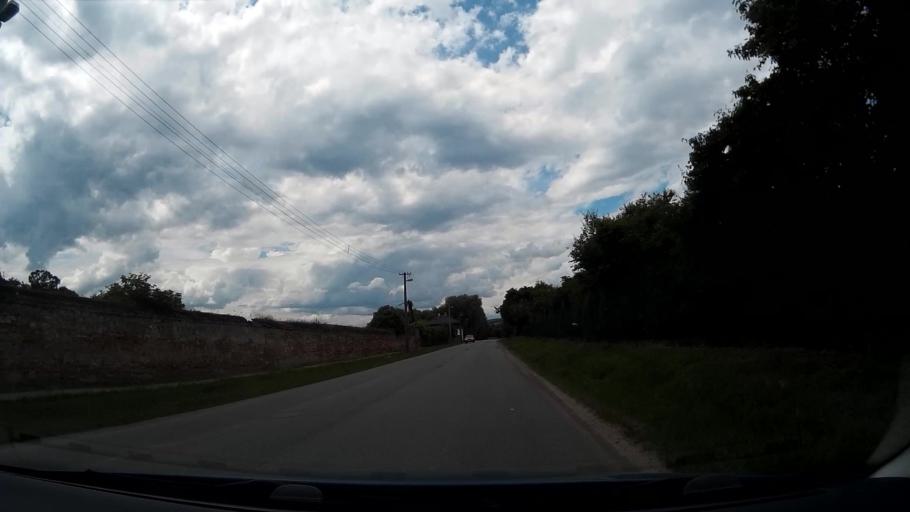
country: CZ
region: South Moravian
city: Troubsko
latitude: 49.1731
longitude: 16.5072
